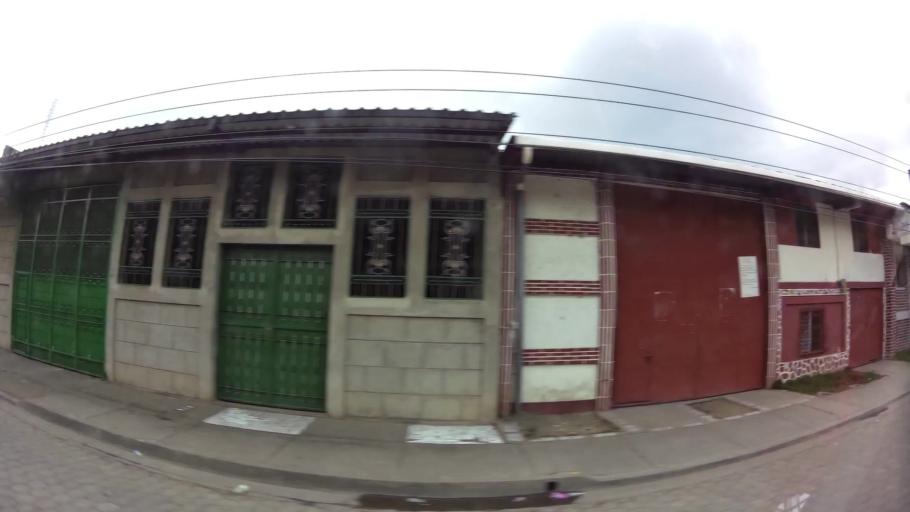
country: NI
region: Jinotega
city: Jinotega
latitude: 13.0956
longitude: -85.9980
